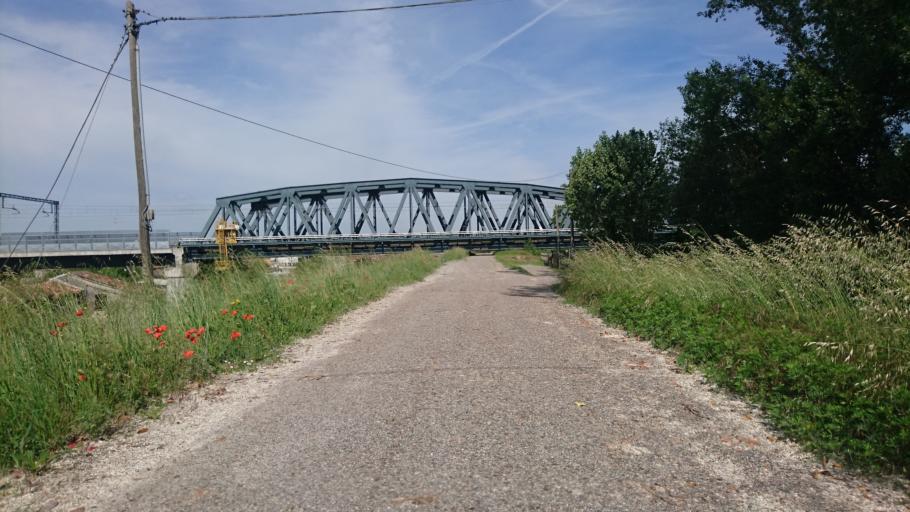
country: IT
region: Lombardy
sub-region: Provincia di Mantova
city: Revere
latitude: 45.0500
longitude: 11.1367
